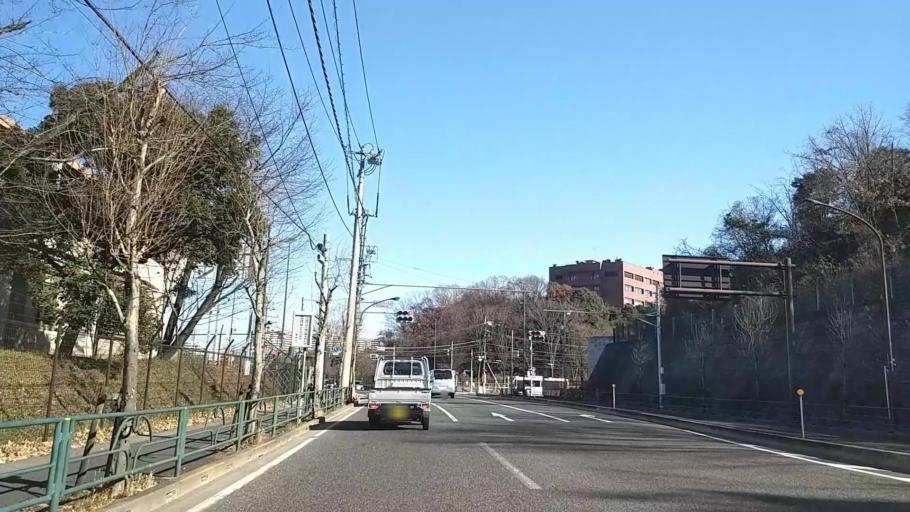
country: JP
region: Tokyo
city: Hachioji
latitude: 35.6309
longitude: 139.2856
